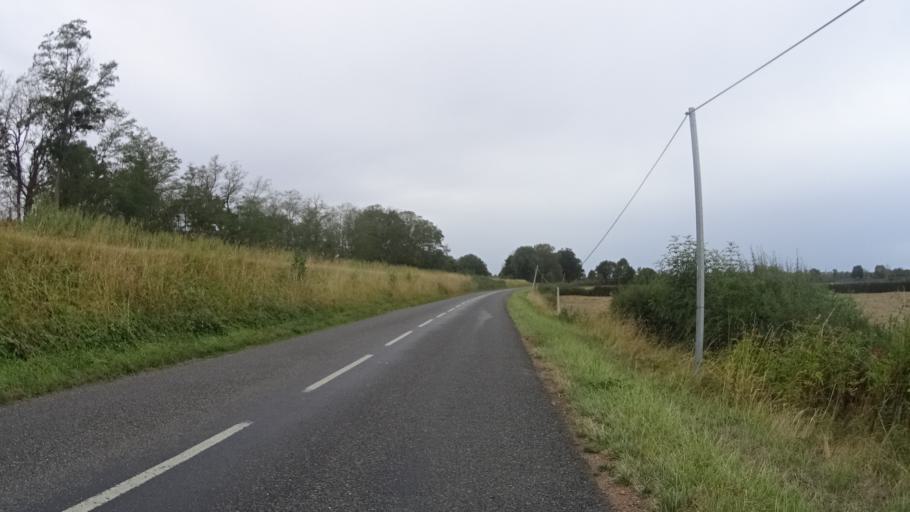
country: FR
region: Bourgogne
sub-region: Departement de la Nievre
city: Decize
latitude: 46.7898
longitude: 3.5145
